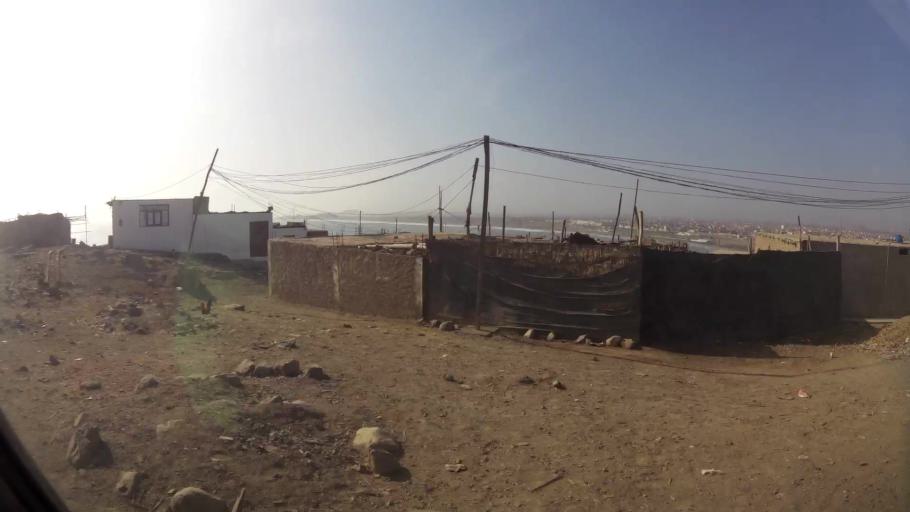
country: PE
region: Lima
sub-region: Huaura
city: Huacho
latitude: -11.1257
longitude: -77.6178
